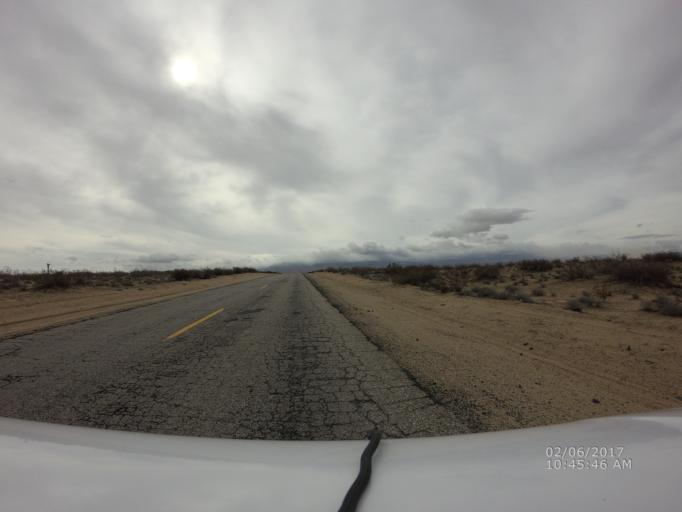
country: US
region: California
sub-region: Los Angeles County
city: Lake Los Angeles
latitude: 34.6336
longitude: -117.7027
